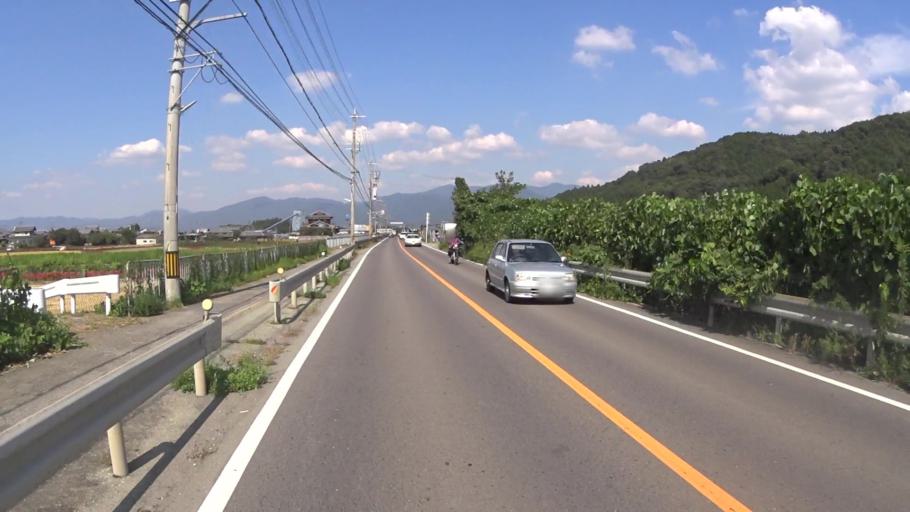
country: JP
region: Kyoto
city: Kameoka
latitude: 35.0009
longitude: 135.5536
